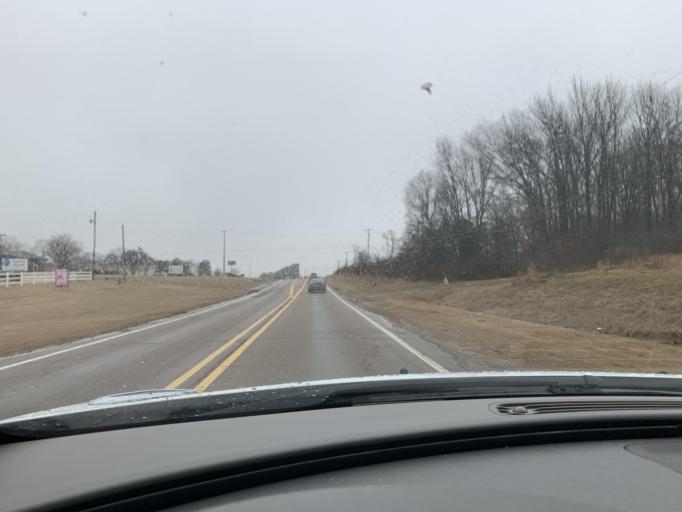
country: US
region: Mississippi
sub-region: De Soto County
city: Horn Lake
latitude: 34.9005
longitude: -89.9971
